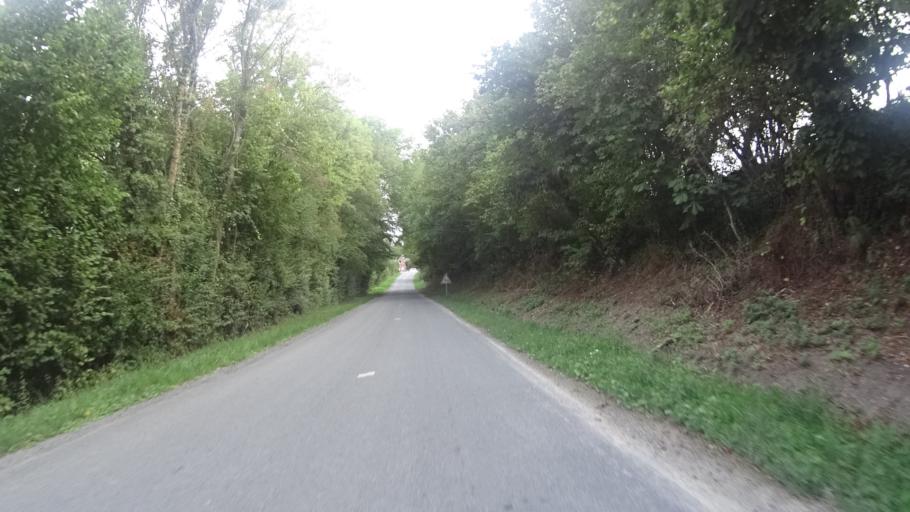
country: FR
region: Picardie
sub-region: Departement de l'Aisne
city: Guise
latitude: 49.9003
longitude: 3.5640
